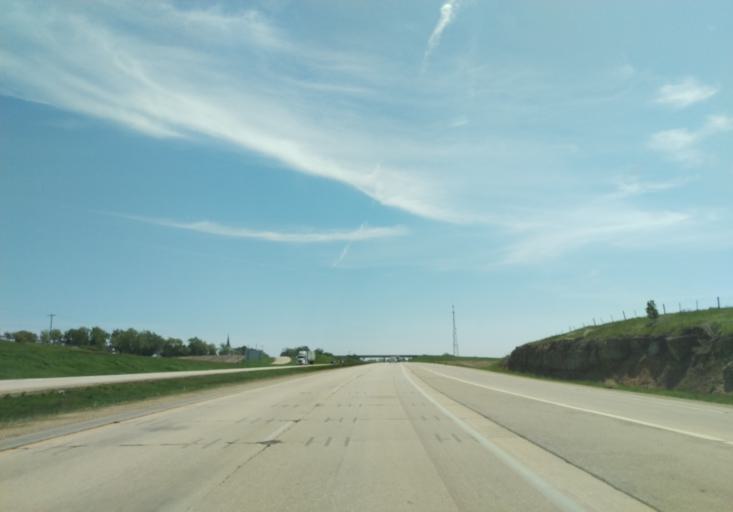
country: US
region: Wisconsin
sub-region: Dane County
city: Mount Horeb
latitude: 43.0048
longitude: -89.6985
